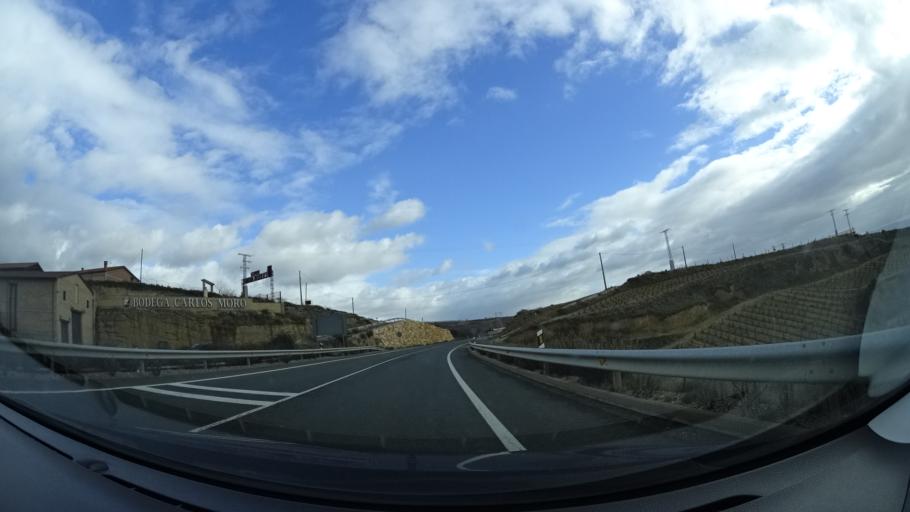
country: ES
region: La Rioja
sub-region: Provincia de La Rioja
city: San Vicente de la Sonsierra
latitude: 42.5715
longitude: -2.7564
